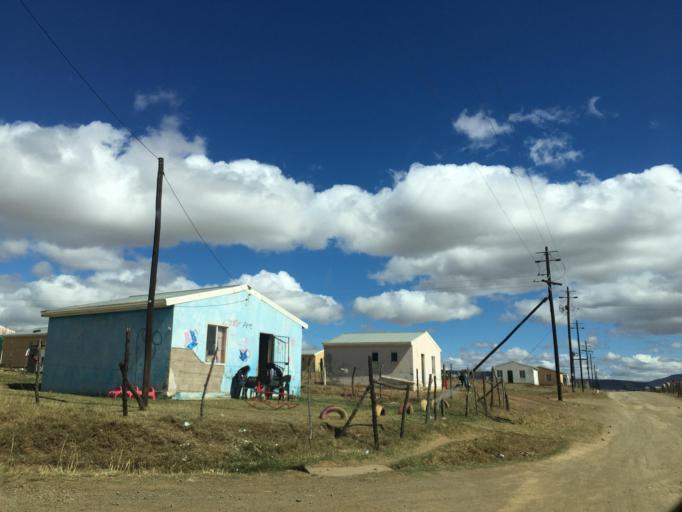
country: ZA
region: Eastern Cape
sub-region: Chris Hani District Municipality
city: Cala
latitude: -31.5405
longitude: 27.6835
